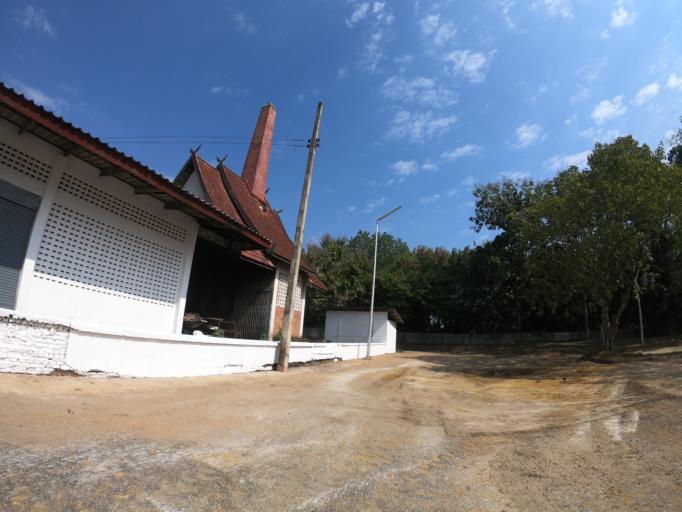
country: TH
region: Chiang Mai
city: Chiang Mai
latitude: 18.8028
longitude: 99.0127
